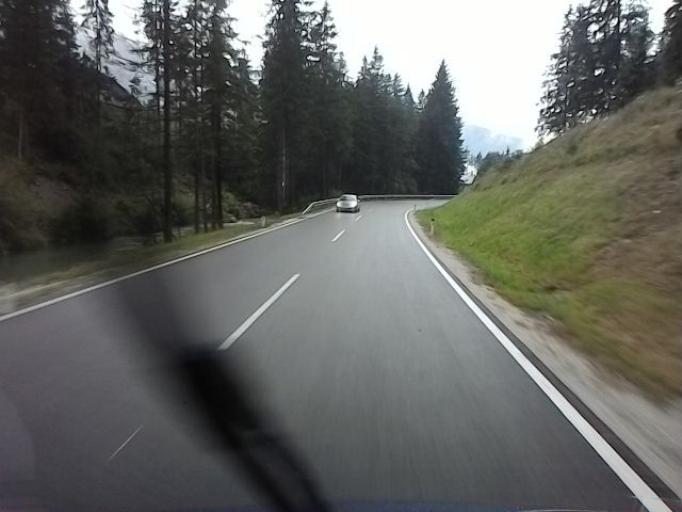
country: AT
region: Tyrol
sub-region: Politischer Bezirk Reutte
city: Ehrwald
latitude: 47.4117
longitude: 10.9132
